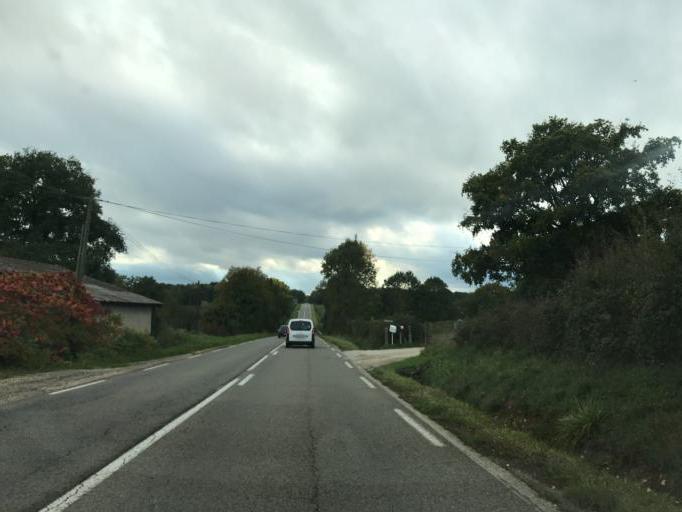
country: FR
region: Rhone-Alpes
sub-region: Departement de l'Ain
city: Buellas
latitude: 46.1834
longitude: 5.0981
